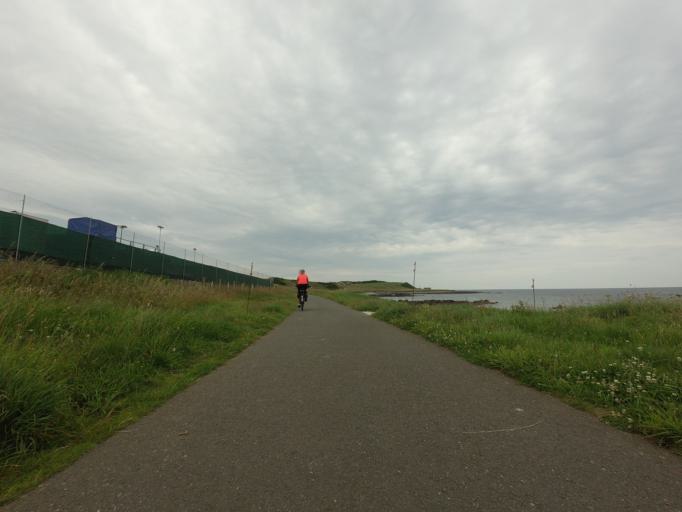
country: GB
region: Scotland
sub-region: Aberdeenshire
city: Whitehills
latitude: 57.6738
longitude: -2.5648
